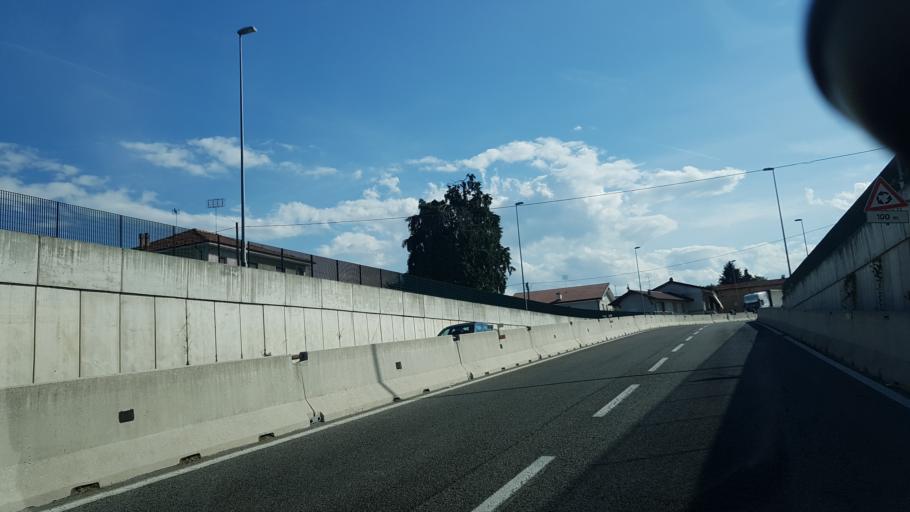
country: IT
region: Piedmont
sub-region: Provincia di Cuneo
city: Cuneo
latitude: 44.3895
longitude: 7.5831
